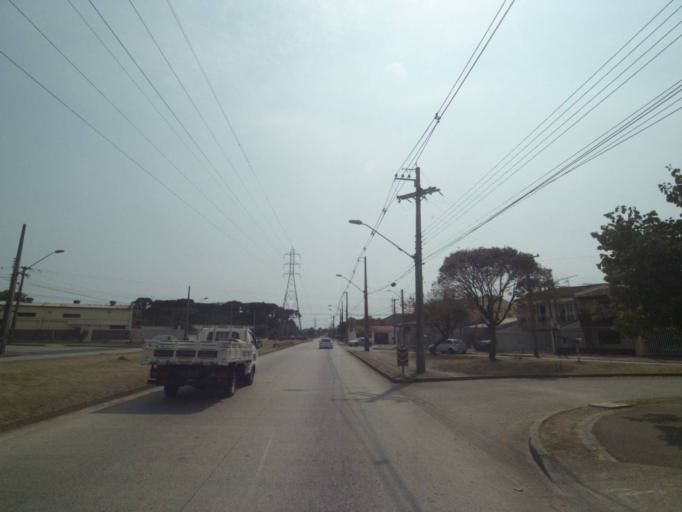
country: BR
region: Parana
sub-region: Sao Jose Dos Pinhais
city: Sao Jose dos Pinhais
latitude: -25.4934
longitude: -49.2079
